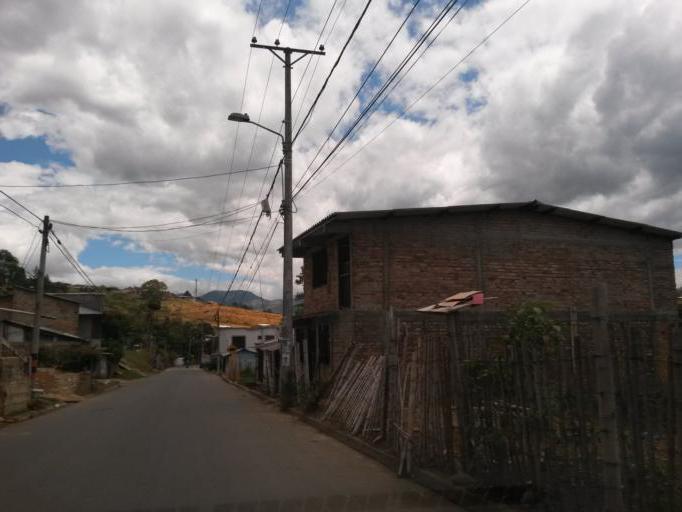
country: CO
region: Cauca
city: Popayan
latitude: 2.4767
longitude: -76.5652
